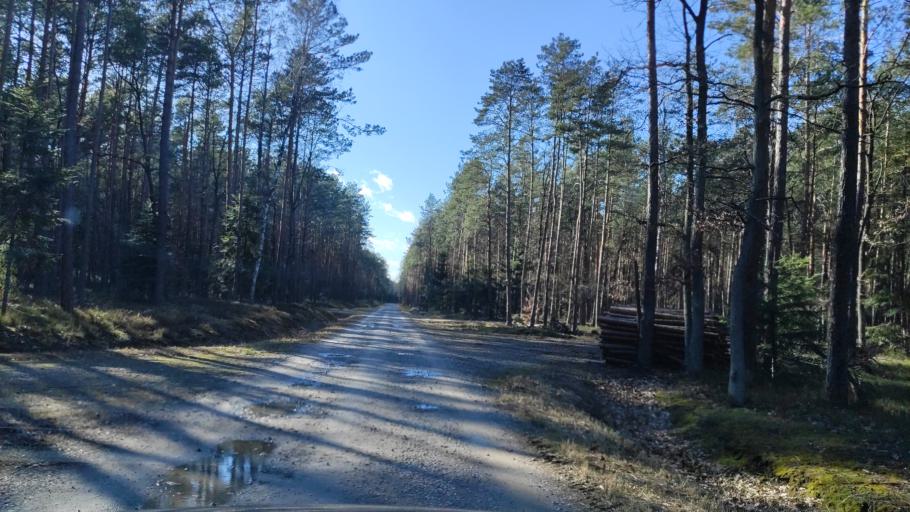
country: PL
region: Masovian Voivodeship
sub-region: Powiat radomski
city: Jastrzebia
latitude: 51.4748
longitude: 21.2836
